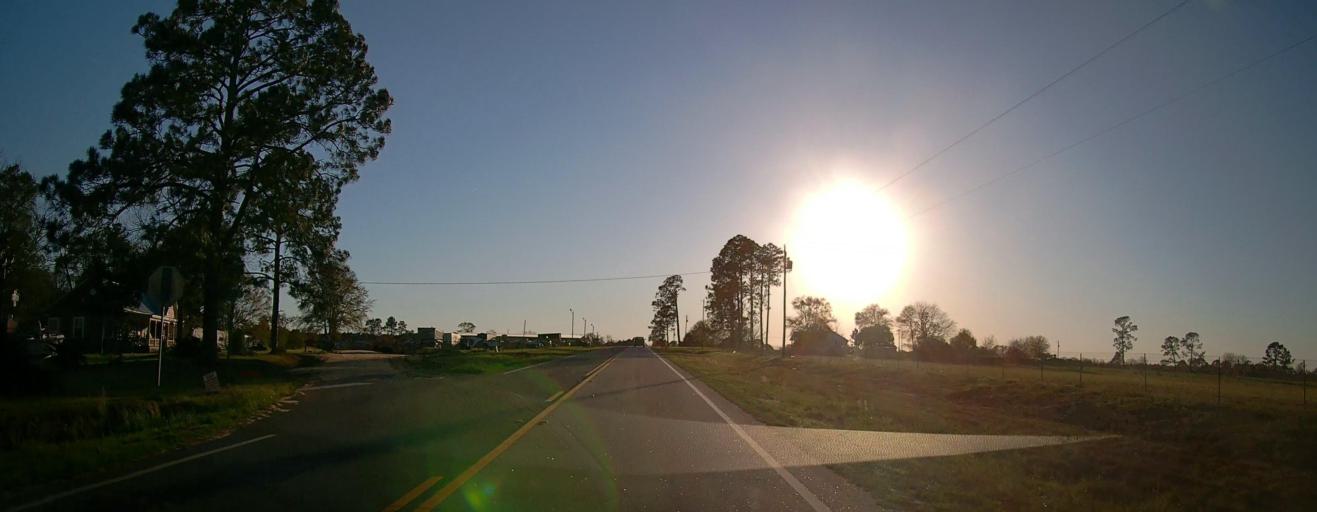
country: US
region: Georgia
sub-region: Wilcox County
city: Rochelle
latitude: 31.9592
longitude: -83.4288
